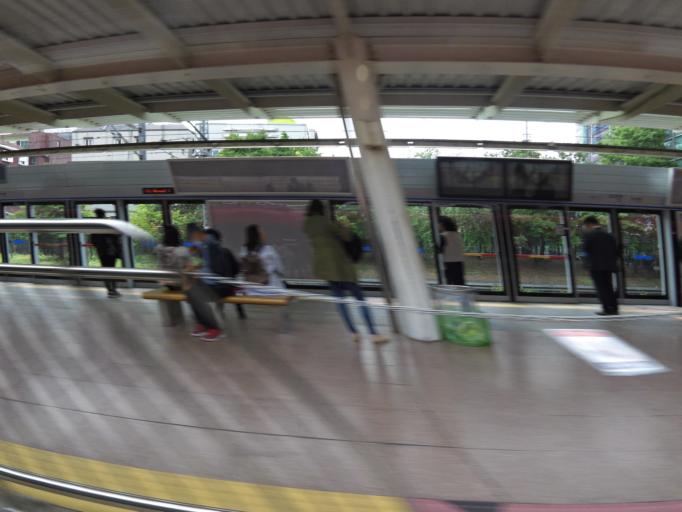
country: KR
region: Gyeonggi-do
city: Anyang-si
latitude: 37.4006
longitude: 126.9236
